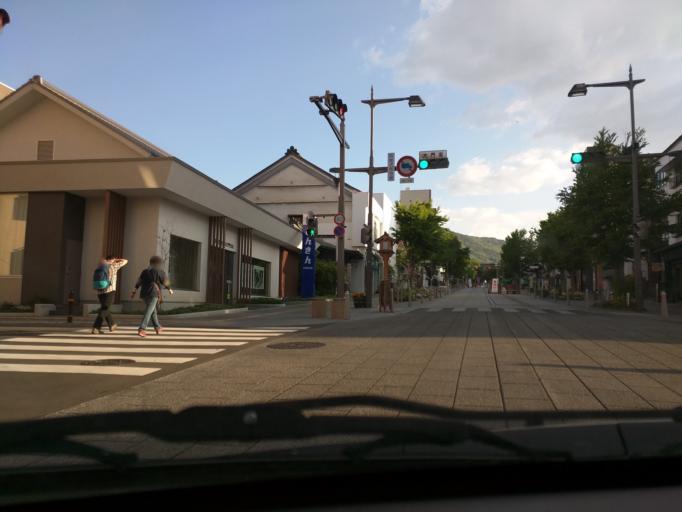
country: JP
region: Nagano
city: Nagano-shi
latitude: 36.6544
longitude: 138.1874
